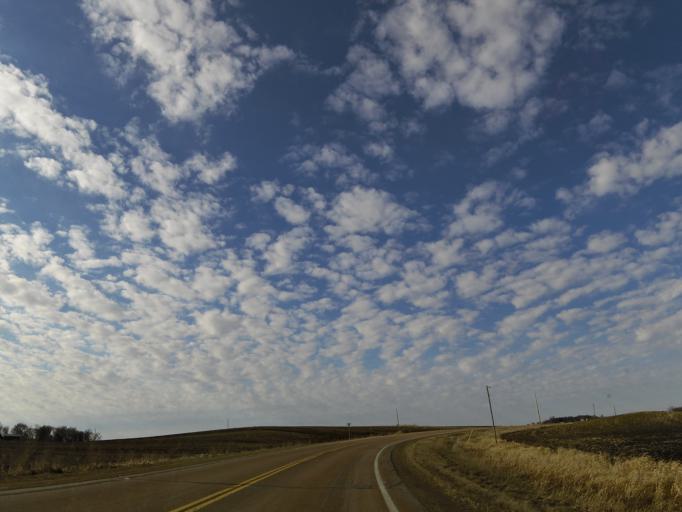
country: US
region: Minnesota
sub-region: Scott County
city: Jordan
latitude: 44.6702
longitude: -93.5207
